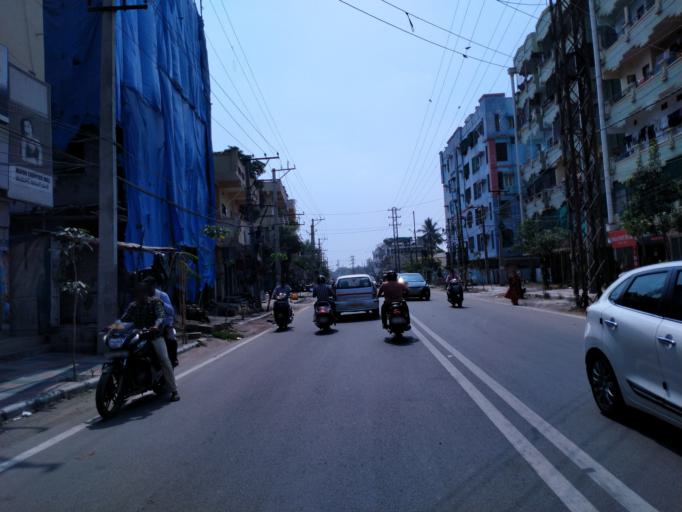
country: IN
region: Telangana
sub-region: Rangareddi
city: Secunderabad
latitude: 17.4805
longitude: 78.5368
